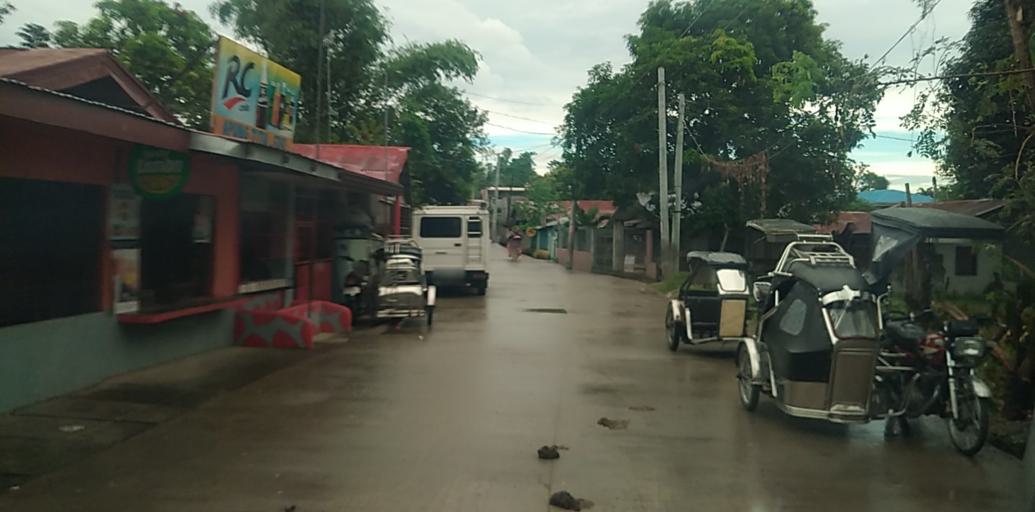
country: PH
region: Central Luzon
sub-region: Province of Pampanga
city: Arayat
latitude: 15.1521
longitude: 120.7463
